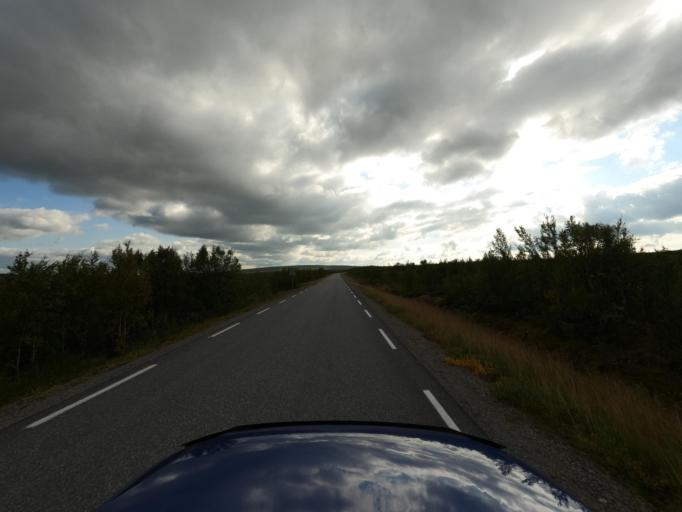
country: NO
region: Finnmark Fylke
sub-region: Porsanger
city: Lakselv
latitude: 69.3740
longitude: 24.2661
